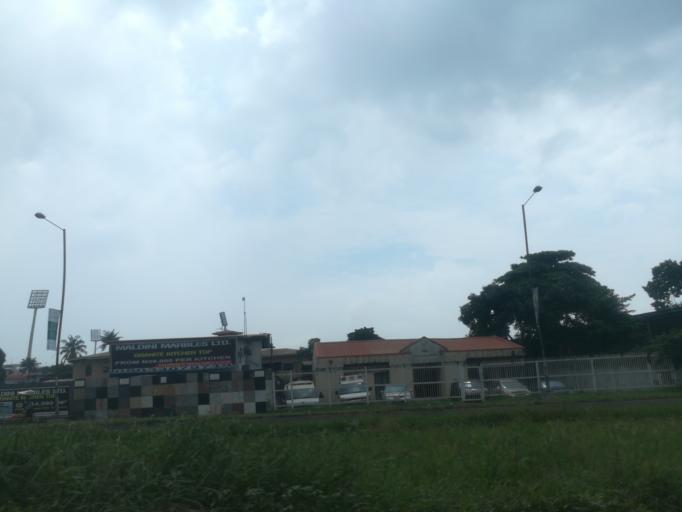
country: NG
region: Lagos
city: Surulere
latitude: 6.4943
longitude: 3.3618
